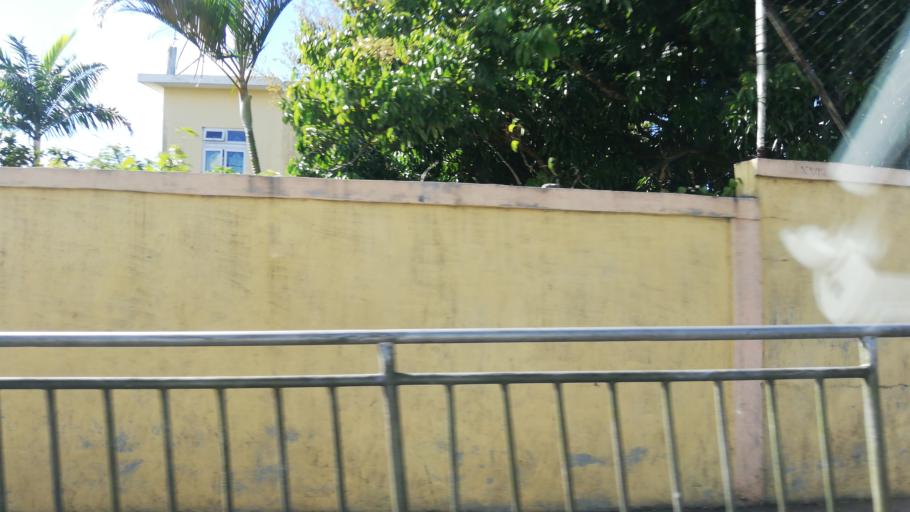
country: MU
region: Moka
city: Quartier Militaire
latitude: -20.2462
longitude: 57.5972
